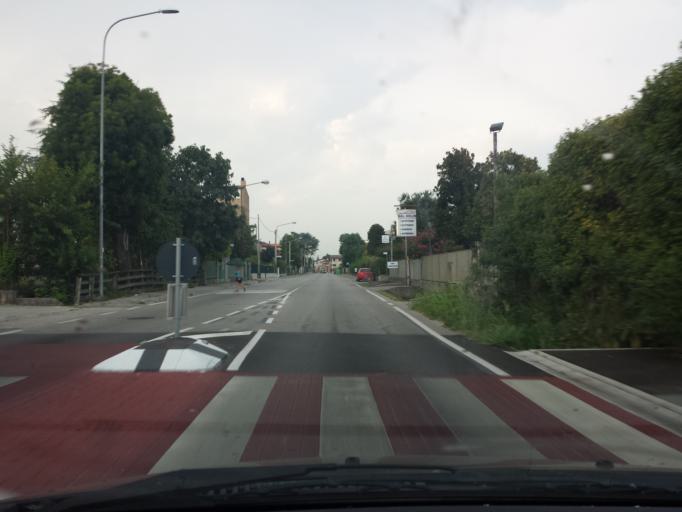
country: IT
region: Veneto
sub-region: Provincia di Vicenza
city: Monticello Conte Otto
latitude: 45.5864
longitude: 11.5561
